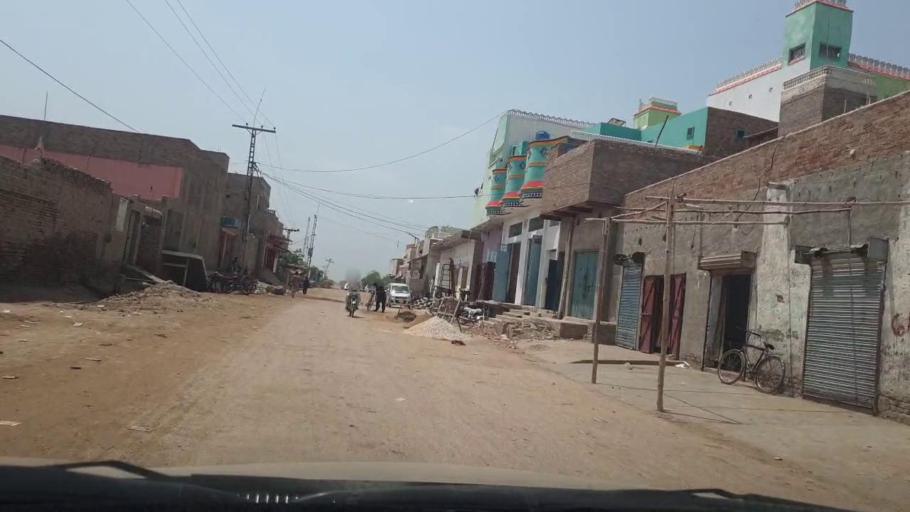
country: PK
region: Sindh
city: Ratodero
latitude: 27.7239
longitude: 68.2812
